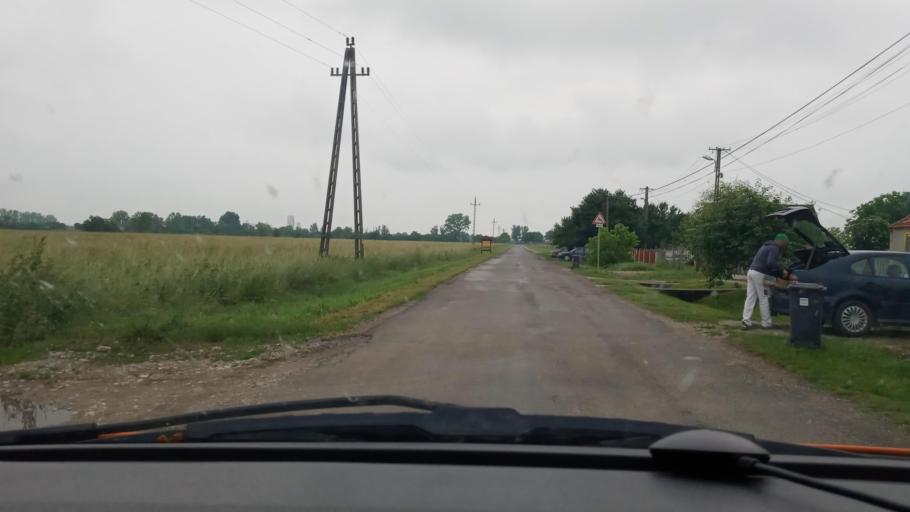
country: HU
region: Baranya
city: Szentlorinc
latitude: 46.0467
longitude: 17.9682
